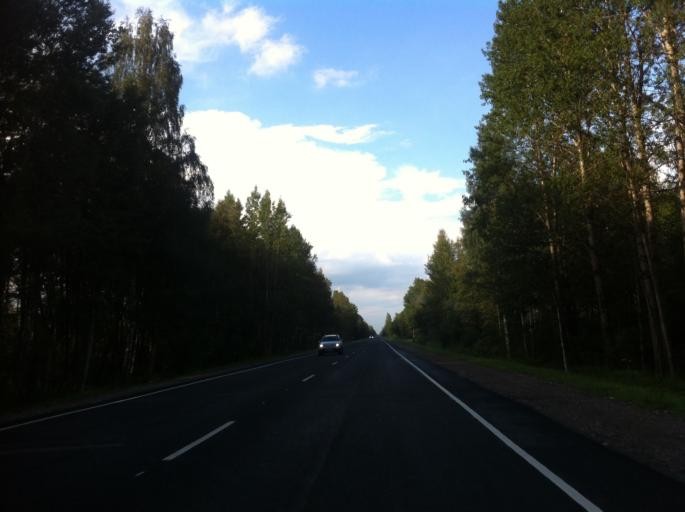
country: RU
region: Leningrad
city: Luga
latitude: 58.4626
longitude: 29.7649
